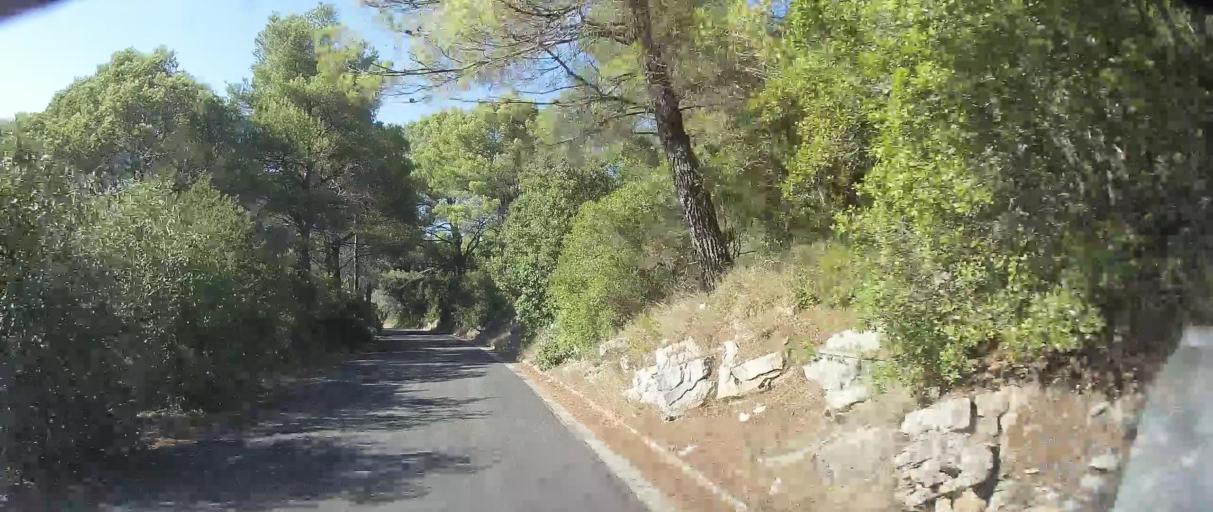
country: HR
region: Dubrovacko-Neretvanska
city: Blato
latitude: 42.7852
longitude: 17.3684
